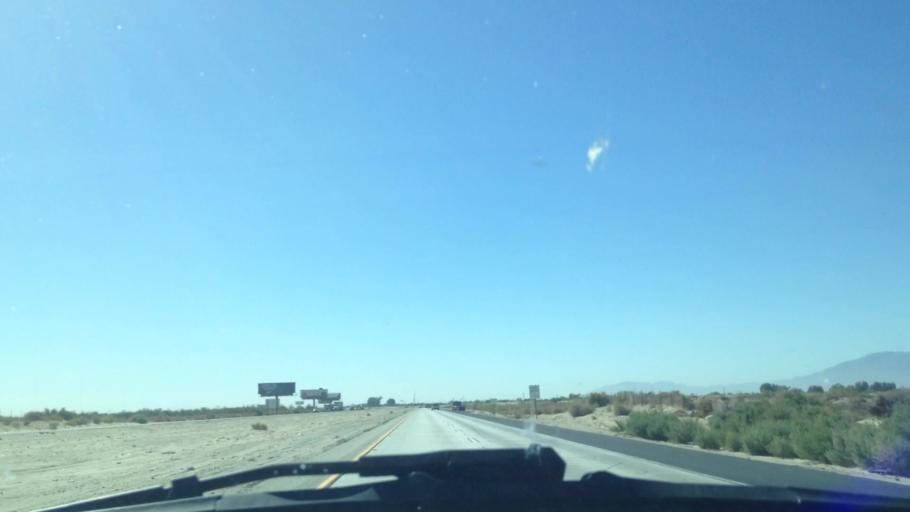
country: US
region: California
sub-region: Riverside County
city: Coachella
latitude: 33.7009
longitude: -116.1756
